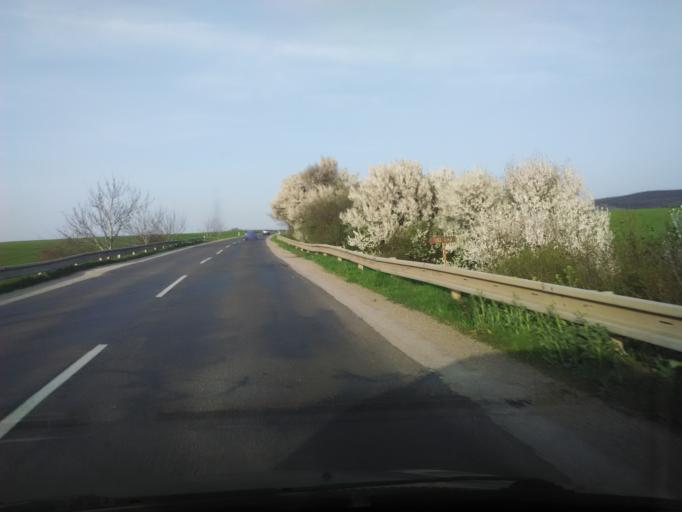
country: SK
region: Nitriansky
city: Surany
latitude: 48.1009
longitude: 18.3203
